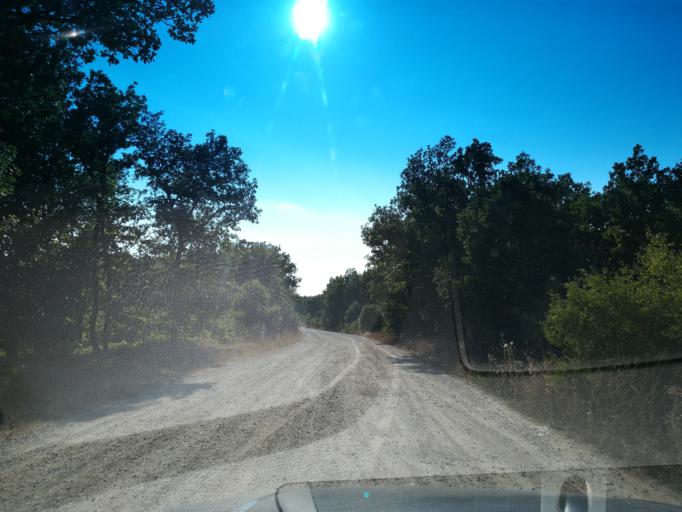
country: BG
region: Khaskovo
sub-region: Obshtina Mineralni Bani
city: Mineralni Bani
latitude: 41.9716
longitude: 25.3301
